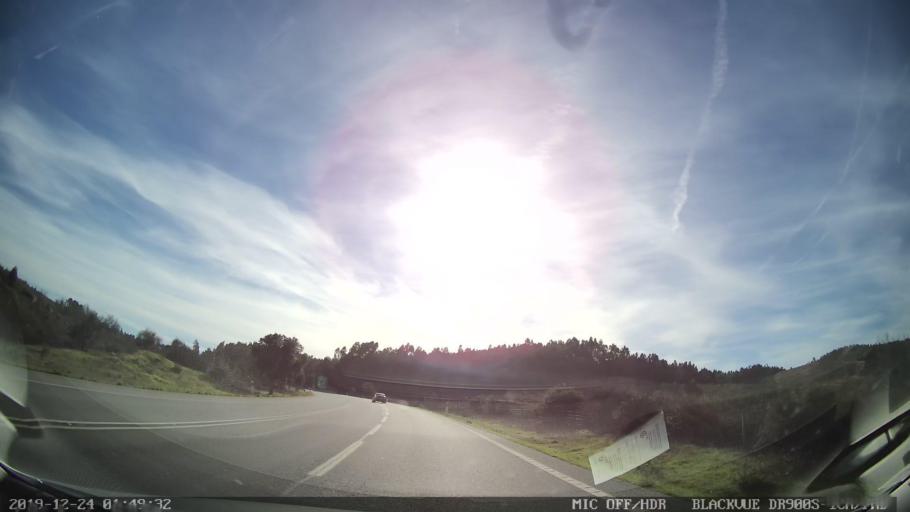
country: PT
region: Portalegre
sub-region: Nisa
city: Nisa
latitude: 39.5072
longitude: -7.7716
